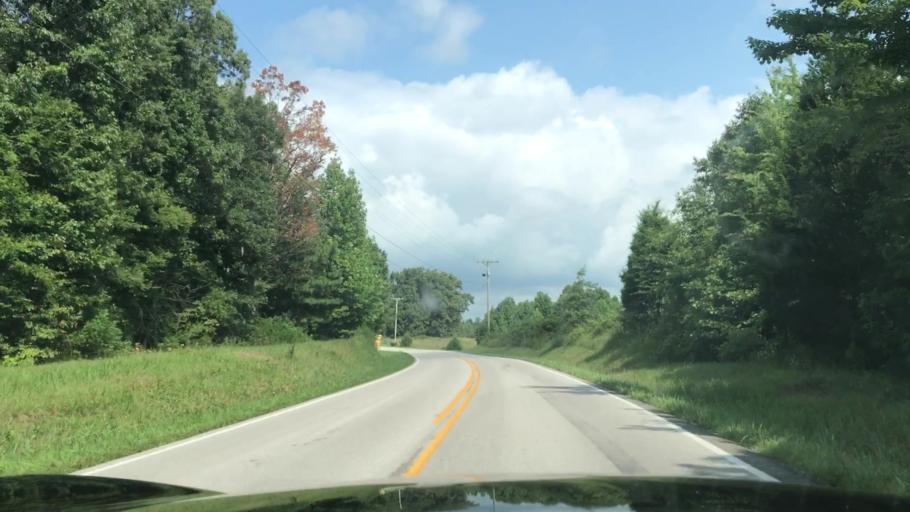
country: US
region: Kentucky
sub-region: Butler County
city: Morgantown
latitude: 37.1889
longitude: -86.8790
